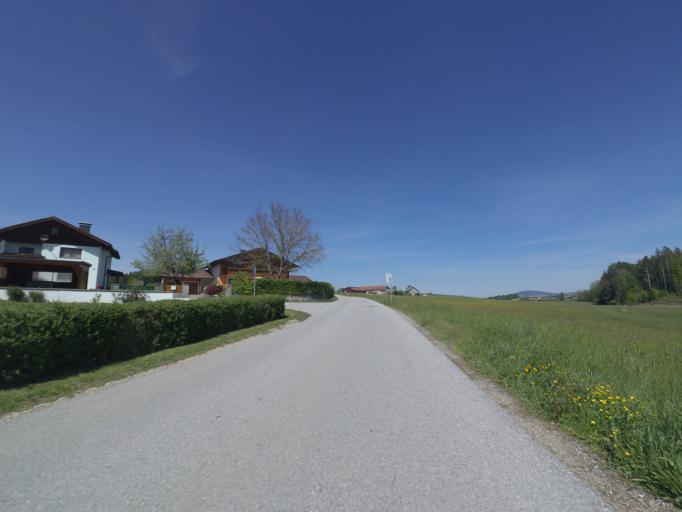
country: AT
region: Salzburg
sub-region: Politischer Bezirk Salzburg-Umgebung
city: Seekirchen am Wallersee
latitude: 47.9114
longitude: 13.1202
